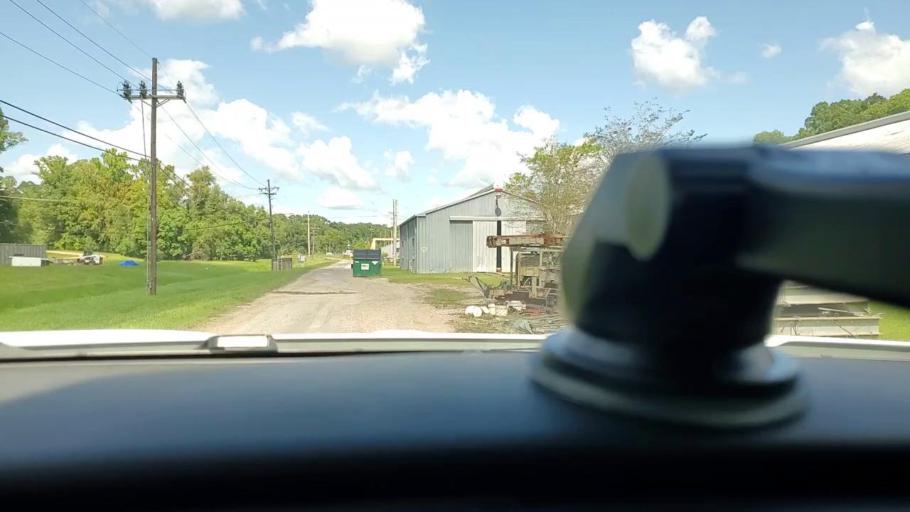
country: US
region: Mississippi
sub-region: Warren County
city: Beechwood
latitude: 32.3062
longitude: -90.8638
